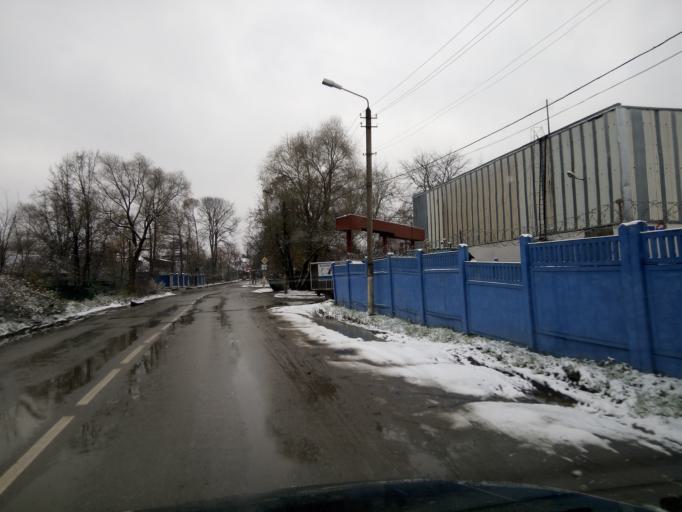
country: RU
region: Moskovskaya
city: Skhodnya
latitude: 55.9464
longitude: 37.2850
